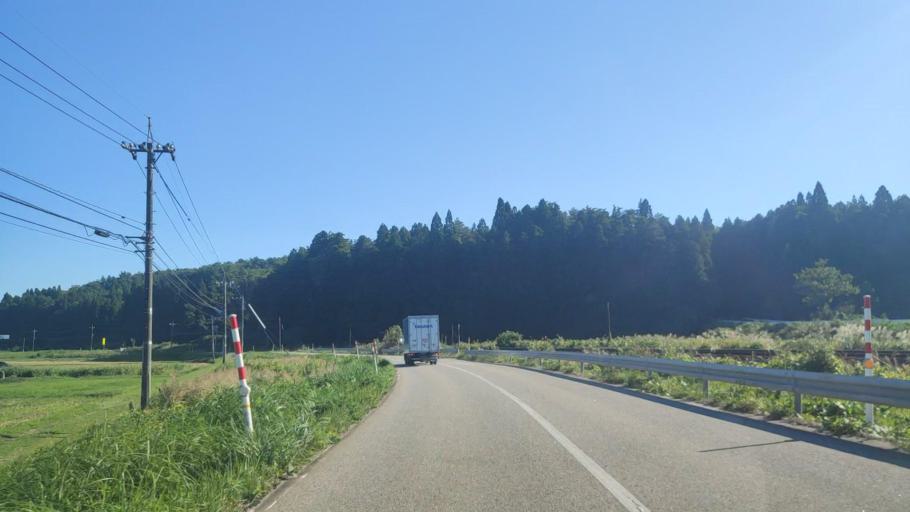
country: JP
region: Ishikawa
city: Nanao
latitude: 37.2024
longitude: 136.9060
